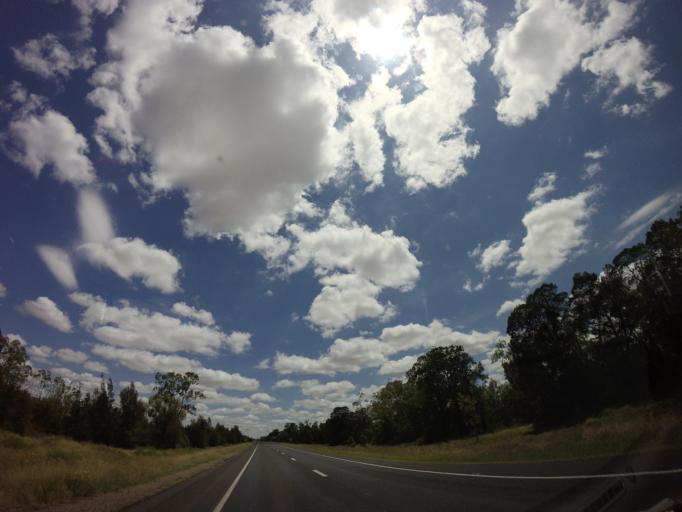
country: AU
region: New South Wales
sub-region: Moree Plains
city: Moree
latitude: -29.1710
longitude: 150.0115
